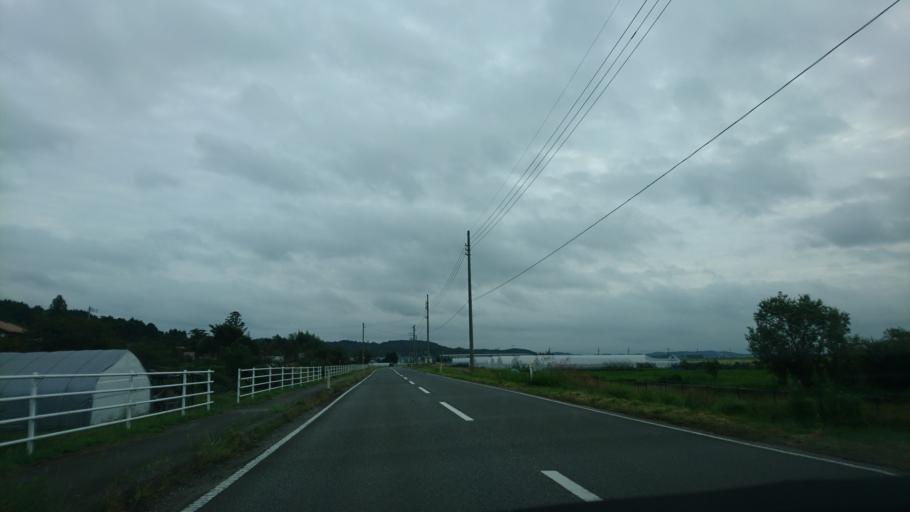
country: JP
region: Iwate
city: Ichinoseki
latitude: 38.8020
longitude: 141.1166
